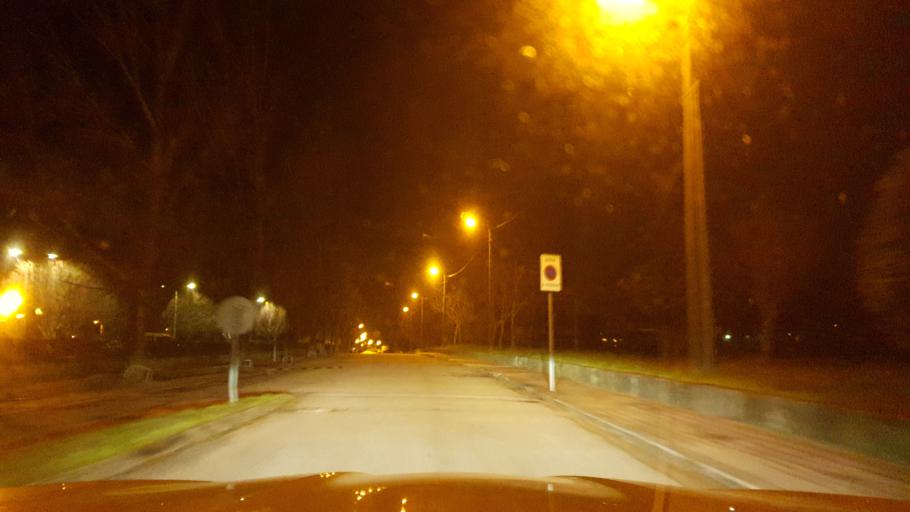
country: PT
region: Porto
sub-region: Maia
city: Leca do Bailio
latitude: 41.2071
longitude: -8.6368
